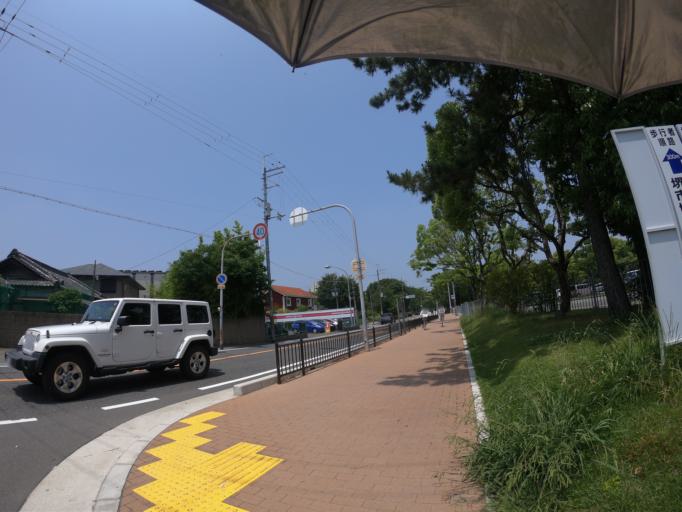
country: JP
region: Osaka
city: Sakai
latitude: 34.5590
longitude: 135.4873
